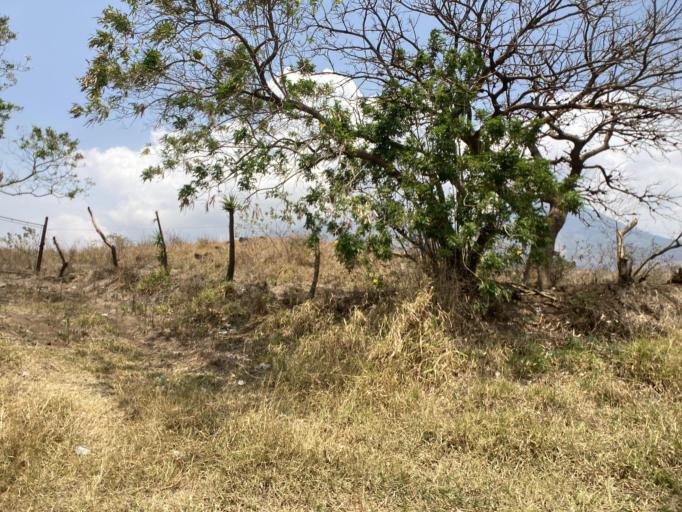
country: GT
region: Escuintla
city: San Vicente Pacaya
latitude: 14.3577
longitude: -90.5715
